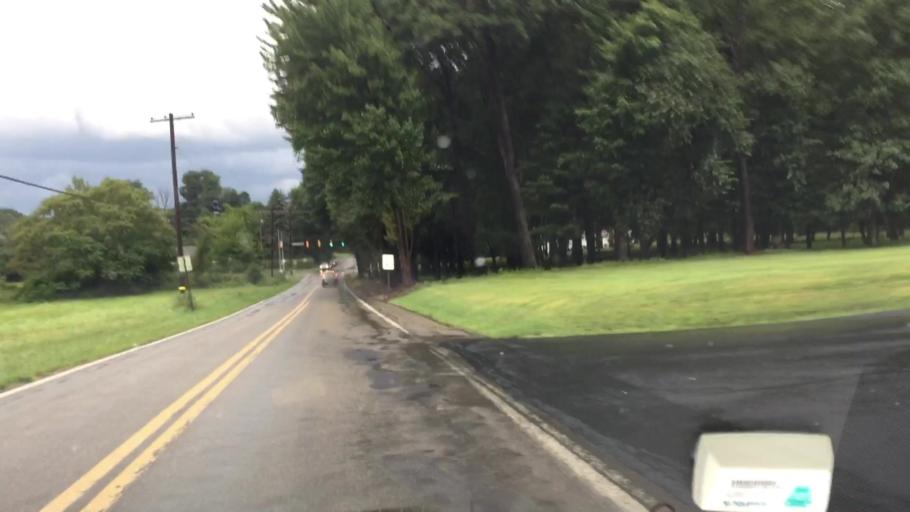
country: US
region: Pennsylvania
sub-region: Butler County
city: Meridian
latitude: 40.8597
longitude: -79.9700
